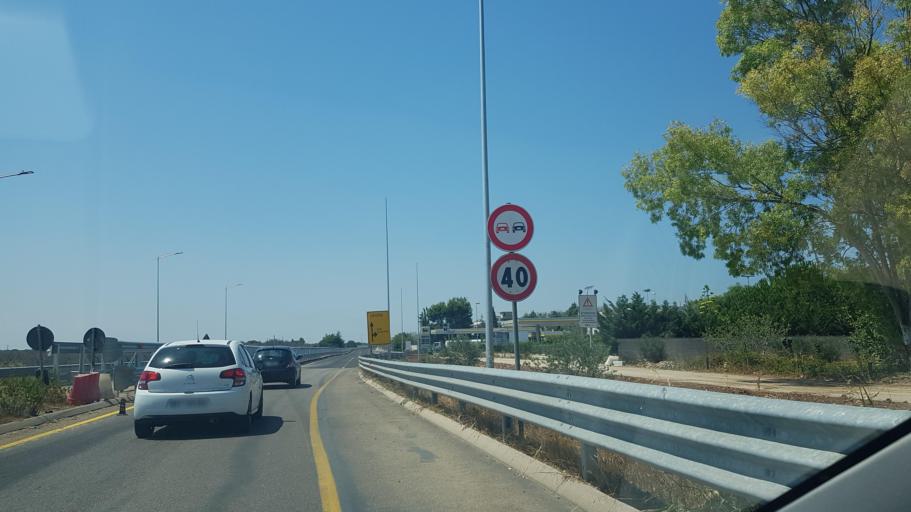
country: IT
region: Apulia
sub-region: Provincia di Lecce
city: Struda
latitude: 40.3154
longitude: 18.2776
